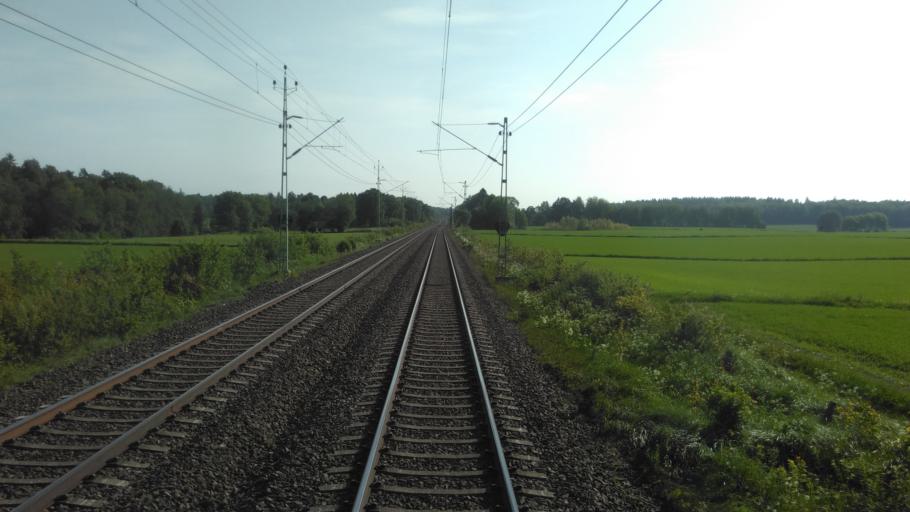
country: SE
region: Vaestra Goetaland
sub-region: Vargarda Kommun
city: Jonstorp
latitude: 58.0009
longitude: 12.6896
